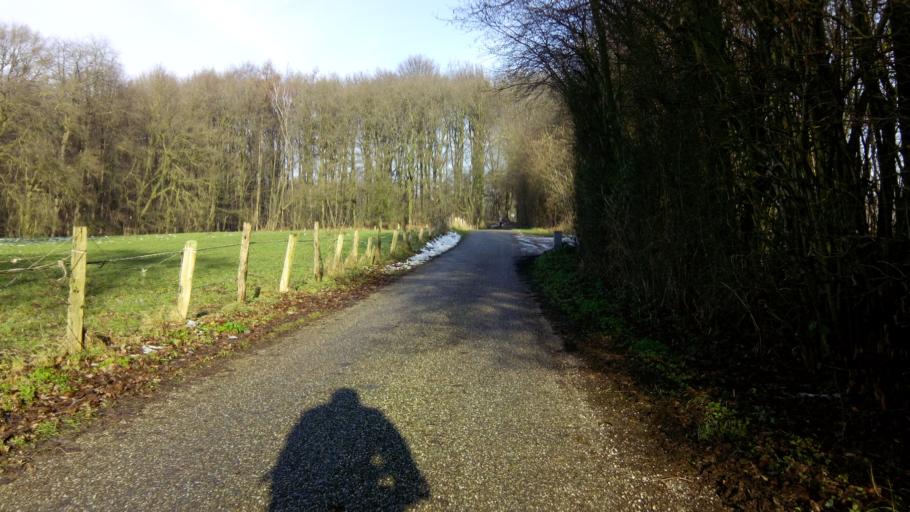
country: NL
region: Gelderland
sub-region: Gemeente Groesbeek
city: Bredeweg
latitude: 51.7492
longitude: 5.9101
